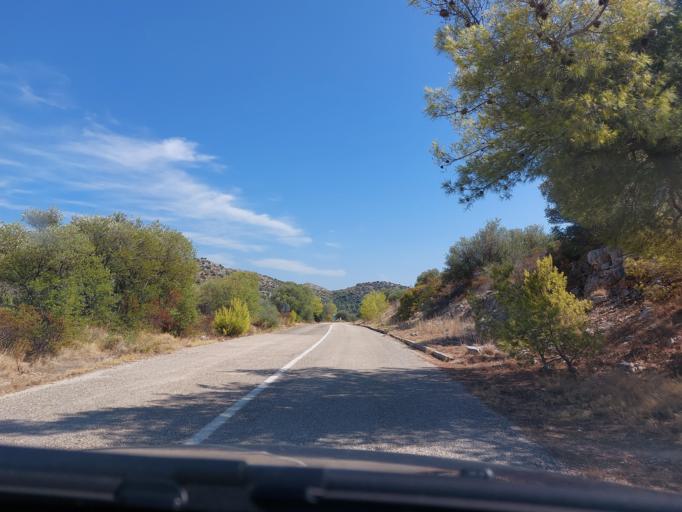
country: HR
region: Dubrovacko-Neretvanska
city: Smokvica
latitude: 42.7406
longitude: 16.8843
